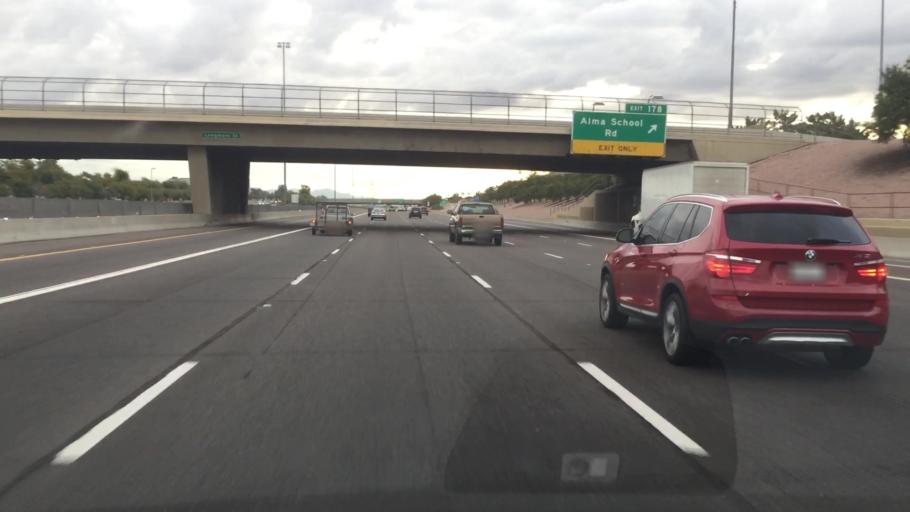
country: US
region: Arizona
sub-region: Maricopa County
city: San Carlos
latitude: 33.3873
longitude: -111.8672
